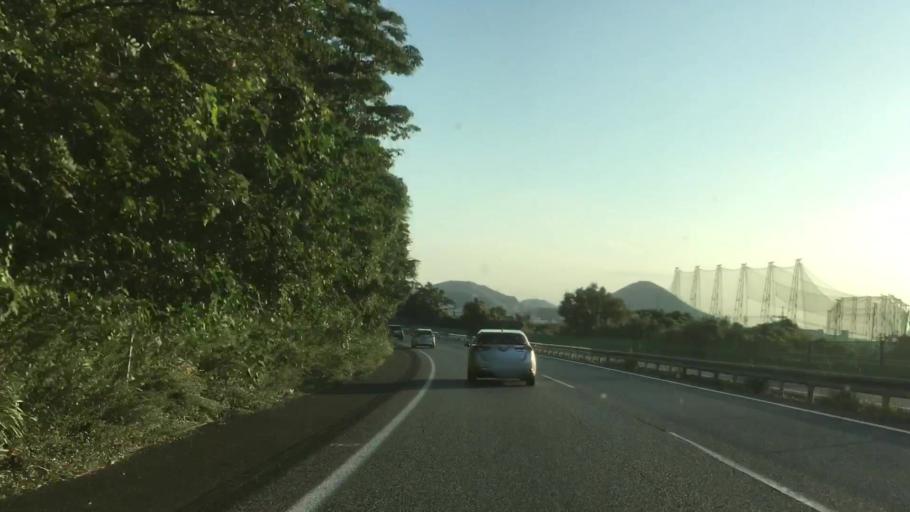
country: JP
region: Yamaguchi
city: Shimonoseki
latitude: 34.0200
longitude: 130.9584
